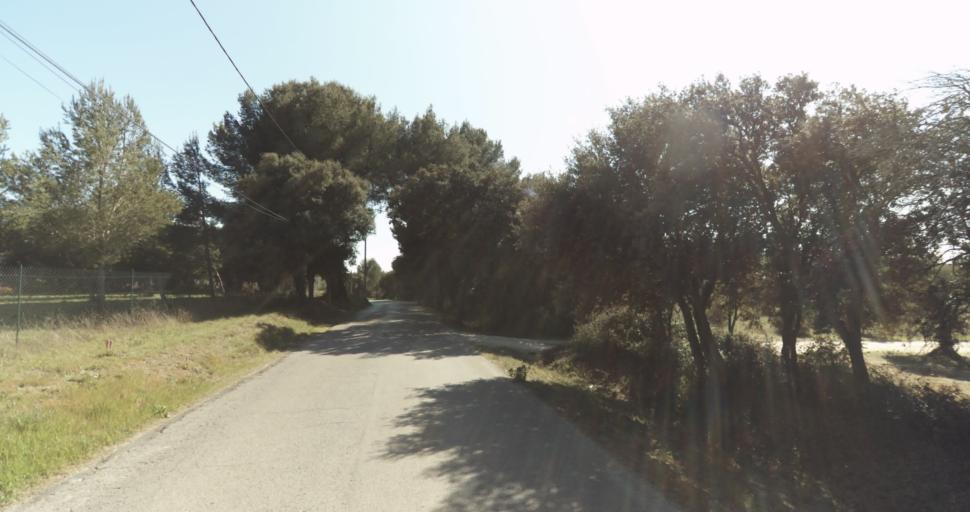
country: FR
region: Provence-Alpes-Cote d'Azur
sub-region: Departement des Bouches-du-Rhone
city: Pelissanne
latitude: 43.6422
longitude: 5.1811
